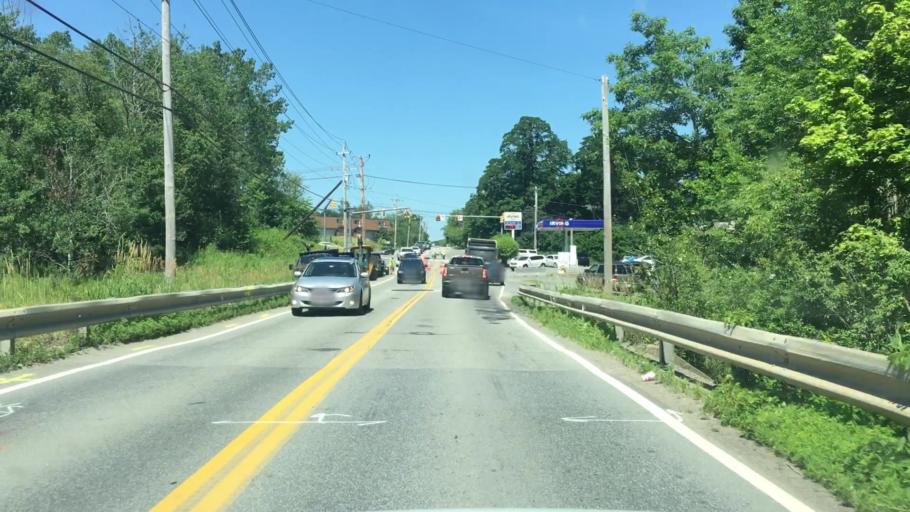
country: US
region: Maine
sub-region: Penobscot County
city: Bangor
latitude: 44.8236
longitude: -68.8080
